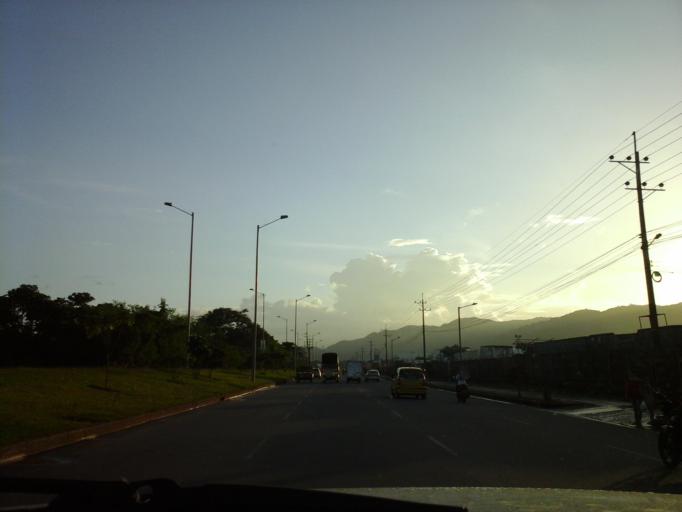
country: CO
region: Meta
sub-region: Villavicencio
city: Villavicencio
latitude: 4.1168
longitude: -73.6256
